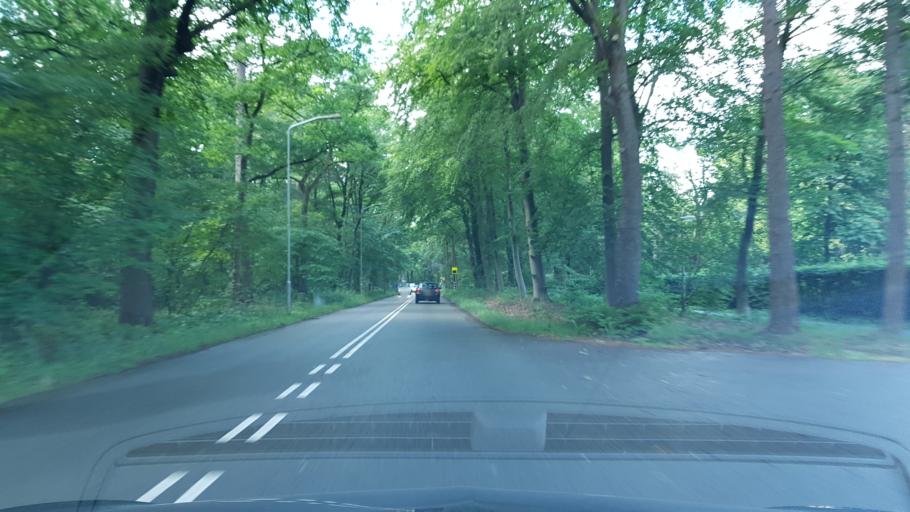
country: NL
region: Gelderland
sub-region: Gemeente Nunspeet
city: Nunspeet
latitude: 52.3788
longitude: 5.8008
